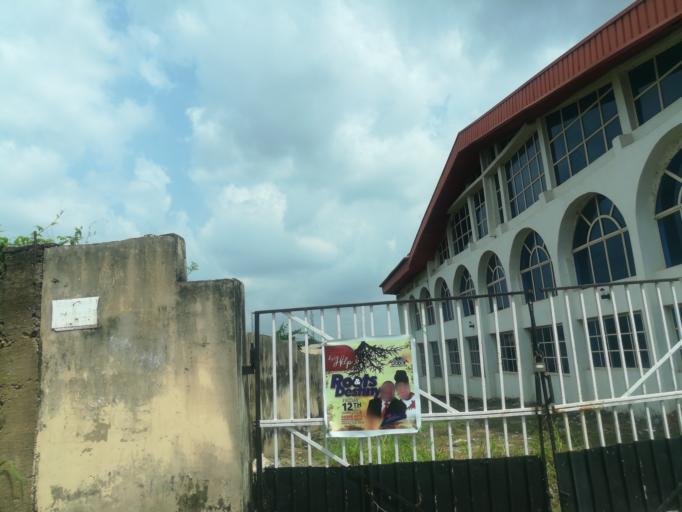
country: NG
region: Oyo
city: Ibadan
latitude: 7.4388
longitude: 3.9406
